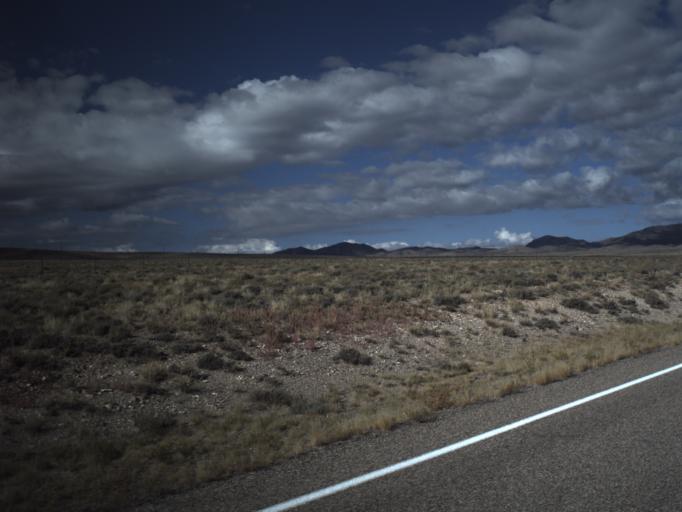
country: US
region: Utah
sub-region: Beaver County
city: Milford
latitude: 38.4294
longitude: -113.1246
